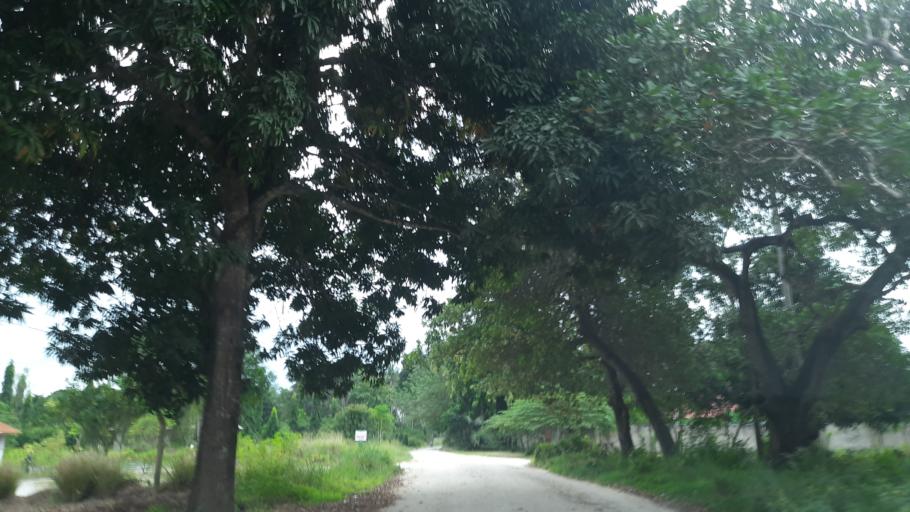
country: TZ
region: Pwani
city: Bagamoyo
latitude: -6.5147
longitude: 38.9299
